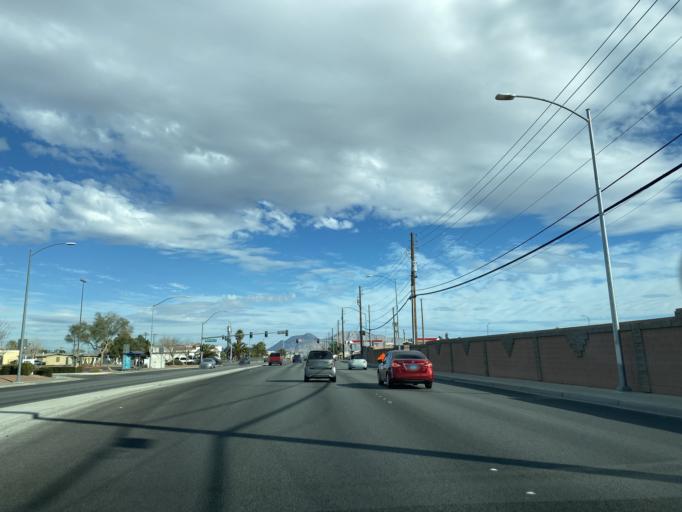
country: US
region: Nevada
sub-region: Clark County
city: Las Vegas
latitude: 36.1884
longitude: -115.1624
